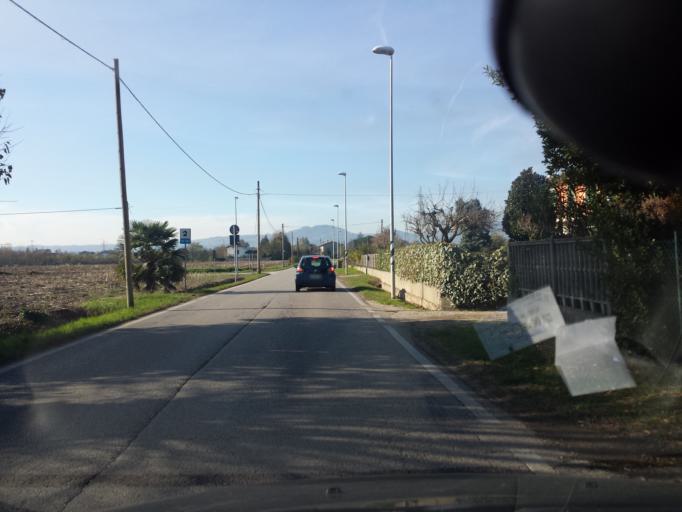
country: IT
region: Veneto
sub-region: Provincia di Vicenza
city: Caldogno-Rettorgole-Cresole
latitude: 45.6100
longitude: 11.5340
